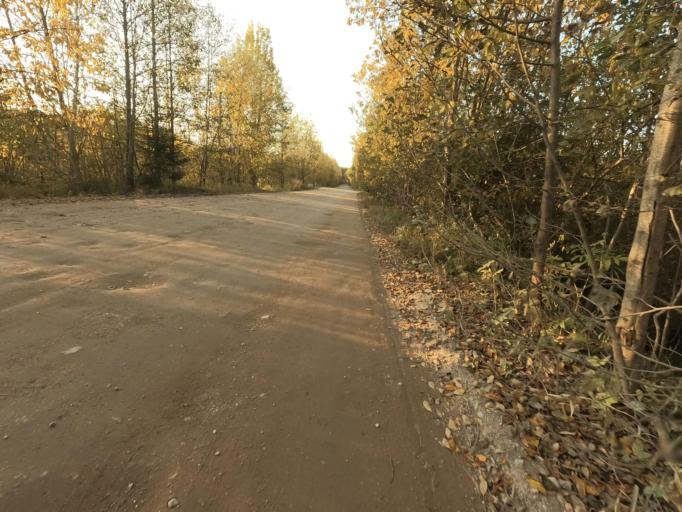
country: RU
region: Leningrad
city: Lyuban'
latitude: 58.9992
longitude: 31.1022
